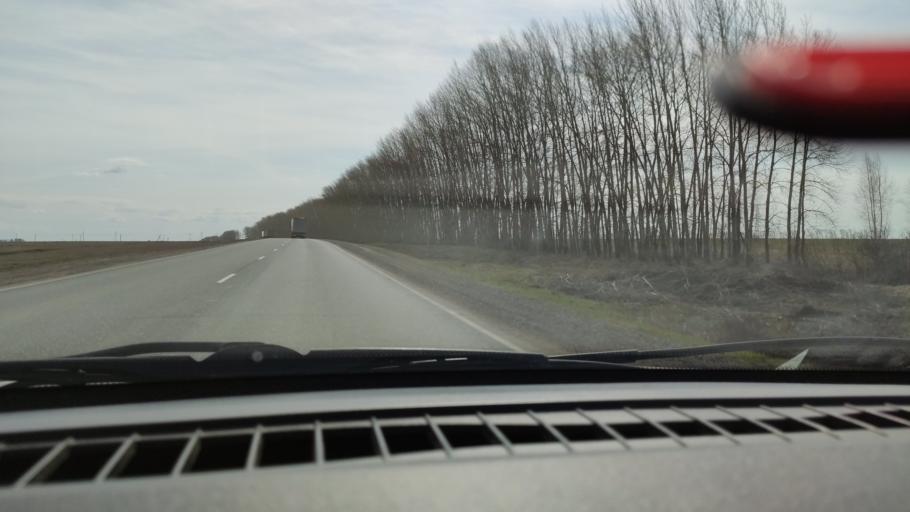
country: RU
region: Bashkortostan
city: Dyurtyuli
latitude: 55.3992
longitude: 54.8314
